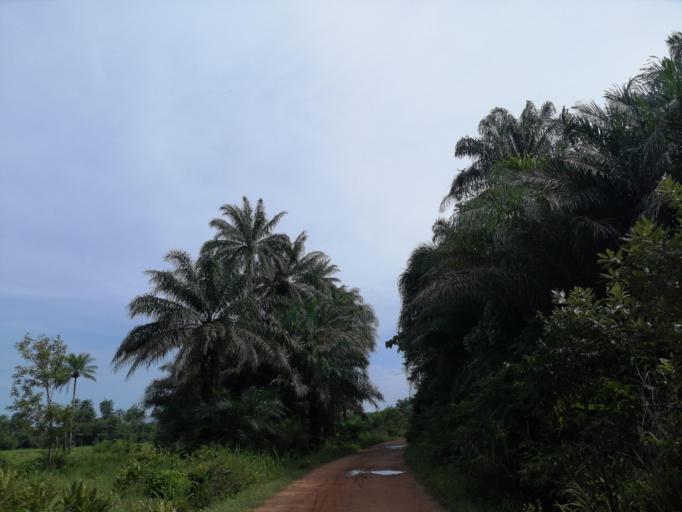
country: SL
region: Northern Province
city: Mange
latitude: 8.8019
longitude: -12.9264
